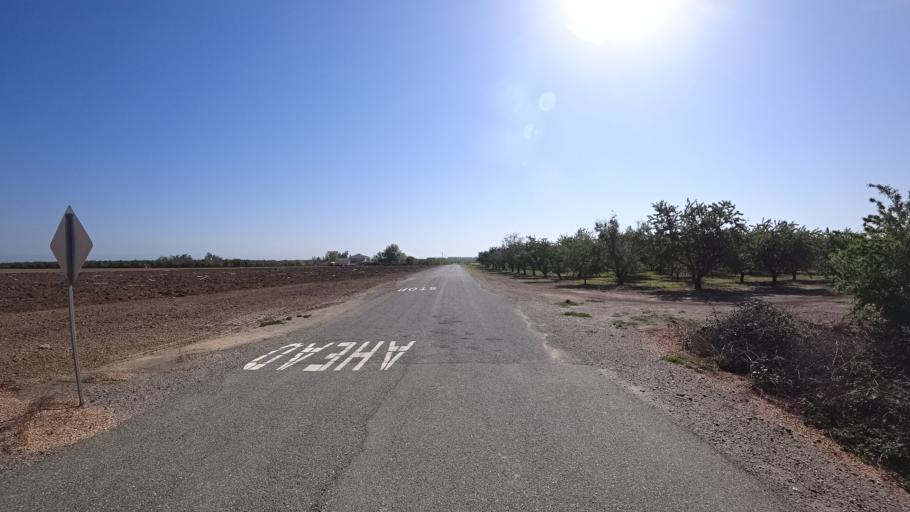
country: US
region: California
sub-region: Glenn County
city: Hamilton City
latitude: 39.6379
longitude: -122.0163
